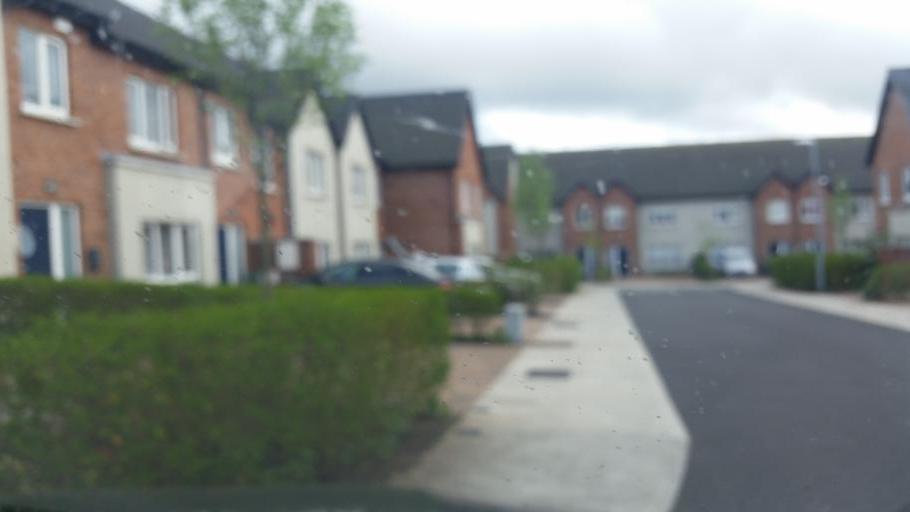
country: IE
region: Leinster
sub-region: Fingal County
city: Blanchardstown
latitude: 53.3926
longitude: -6.3650
